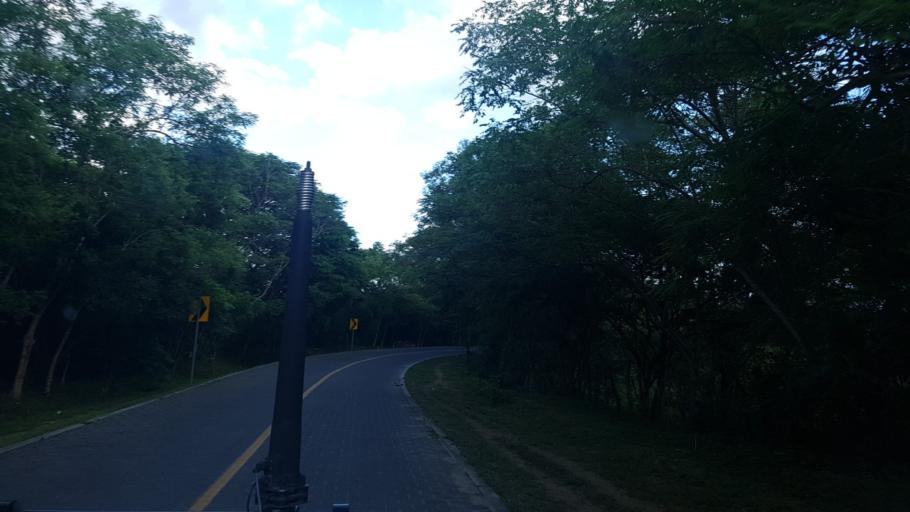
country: NI
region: Nueva Segovia
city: Ocotal
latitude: 13.6459
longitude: -86.6048
